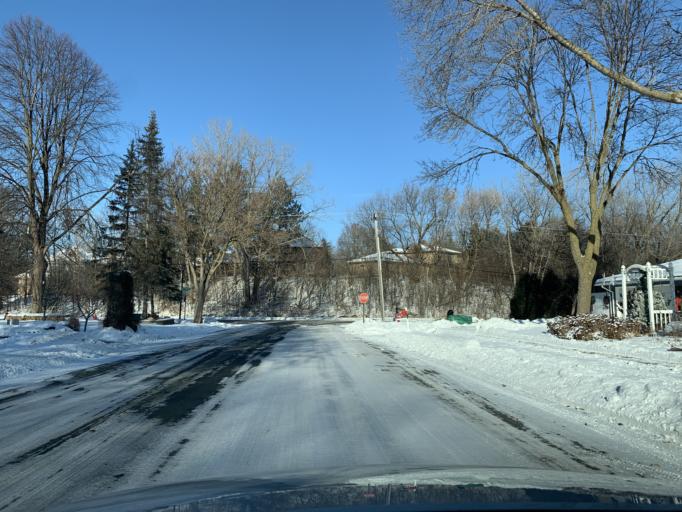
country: US
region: Minnesota
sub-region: Scott County
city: Savage
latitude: 44.8325
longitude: -93.3546
